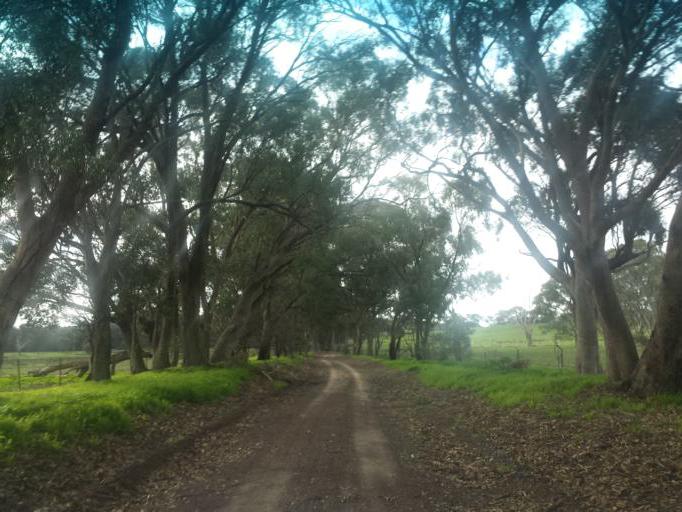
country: AU
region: Victoria
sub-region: Murrindindi
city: Kinglake West
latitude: -37.0202
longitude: 145.2502
